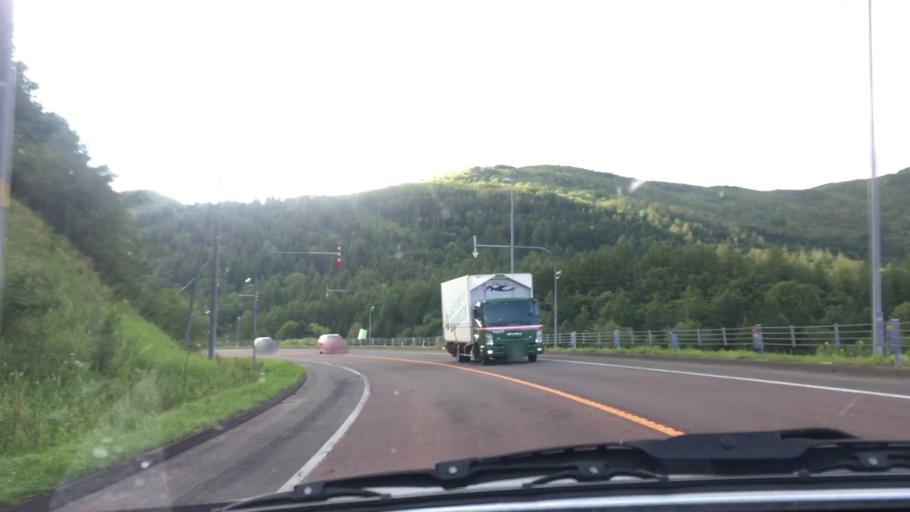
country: JP
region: Hokkaido
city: Shimo-furano
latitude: 43.1380
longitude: 142.7528
